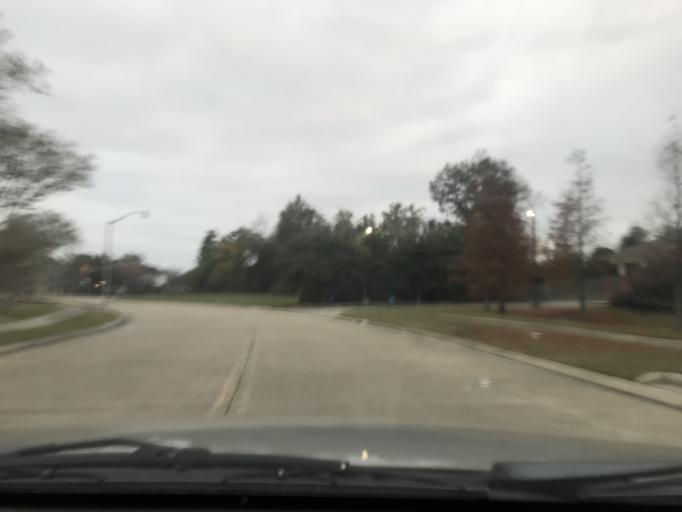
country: US
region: Louisiana
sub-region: Jefferson Parish
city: Woodmere
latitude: 29.8742
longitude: -90.0906
